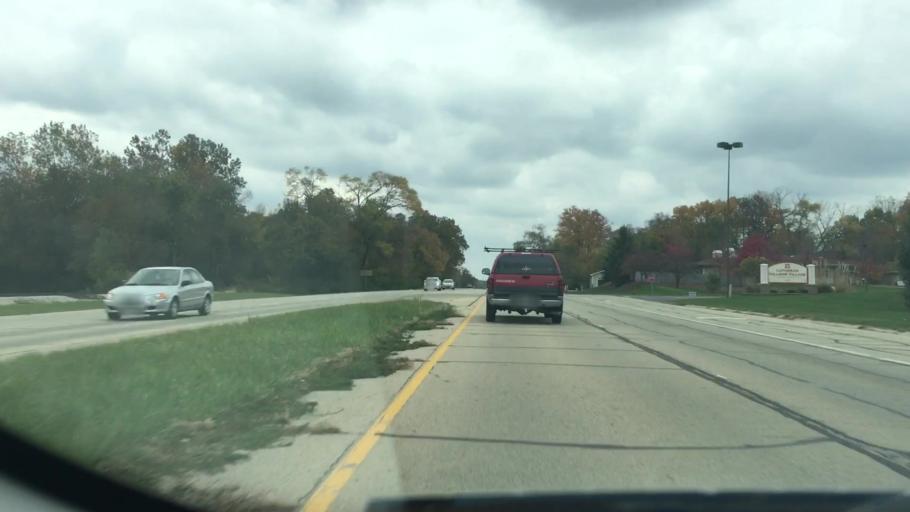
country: US
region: Illinois
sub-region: Peoria County
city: Peoria Heights
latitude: 40.7709
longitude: -89.5729
